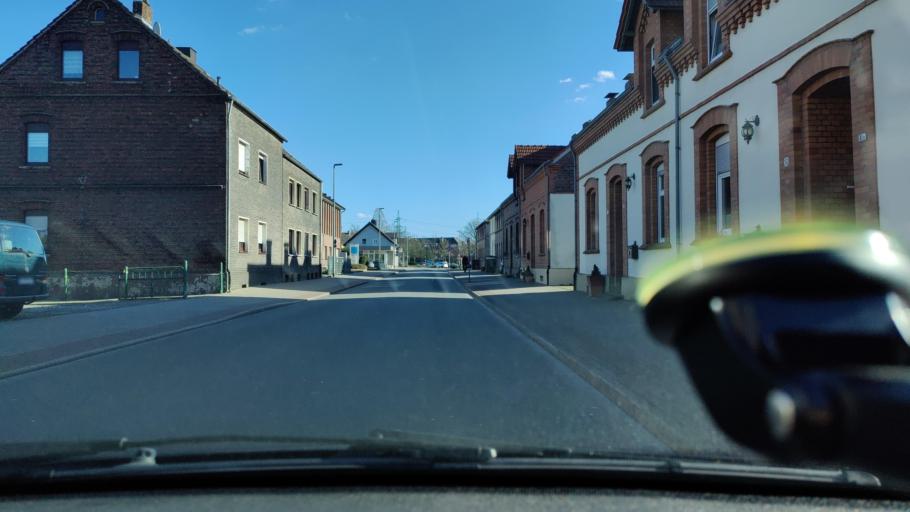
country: DE
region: North Rhine-Westphalia
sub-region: Regierungsbezirk Dusseldorf
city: Dinslaken
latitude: 51.5720
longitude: 6.7472
